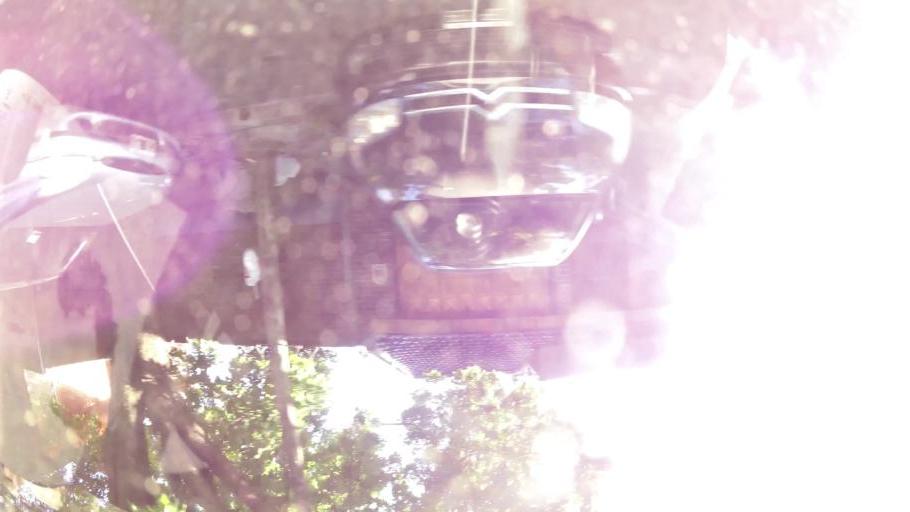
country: AR
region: Buenos Aires
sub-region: Partido de General San Martin
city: General San Martin
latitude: -34.5703
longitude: -58.5493
